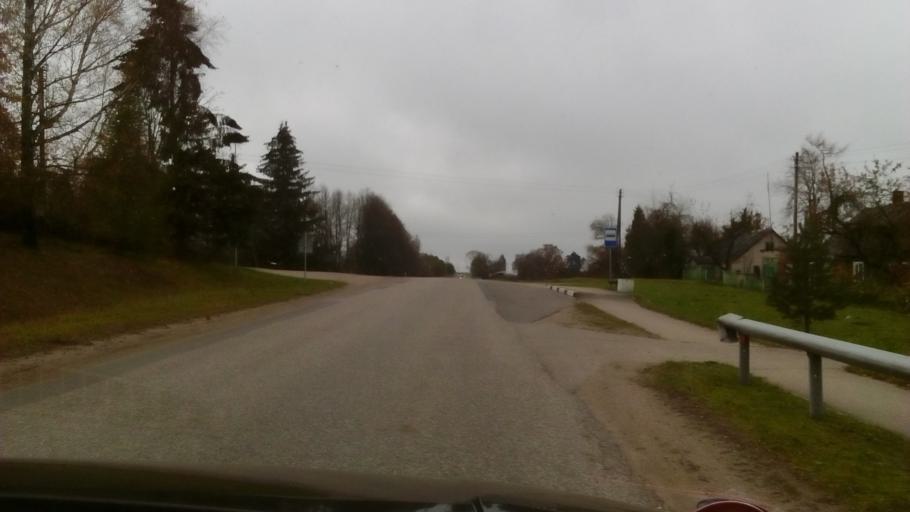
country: LT
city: Simnas
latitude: 54.3727
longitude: 23.5295
